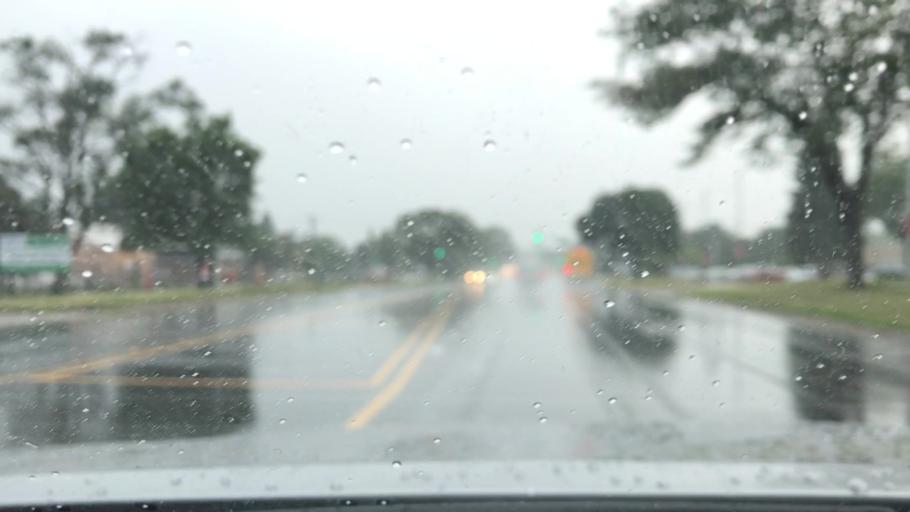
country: US
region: Illinois
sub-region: DuPage County
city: Lisle
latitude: 41.7987
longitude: -88.0955
